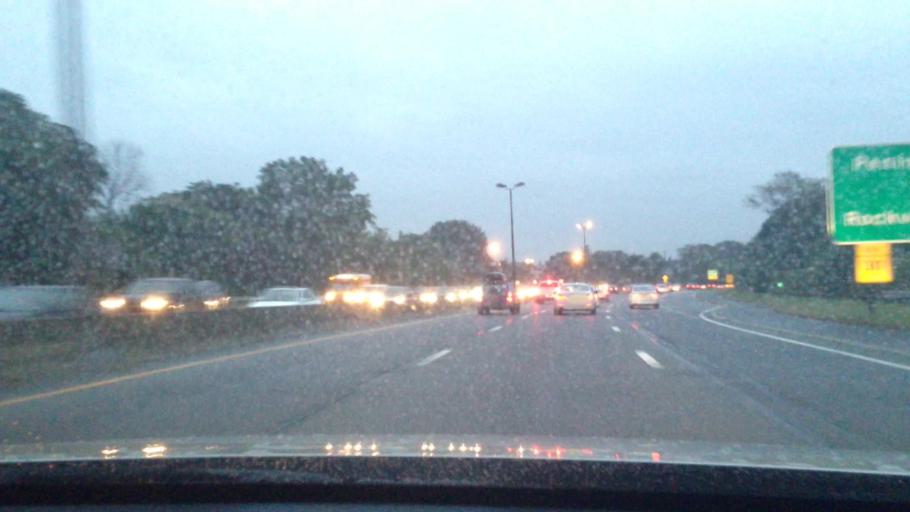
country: US
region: New York
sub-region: Nassau County
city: Lakeview
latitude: 40.6887
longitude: -73.6374
